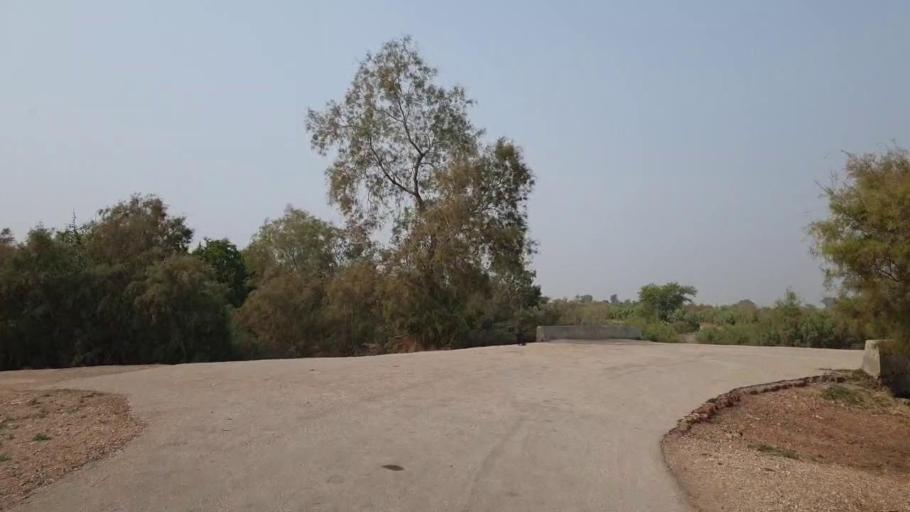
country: PK
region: Sindh
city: Bhan
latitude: 26.4899
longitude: 67.7007
